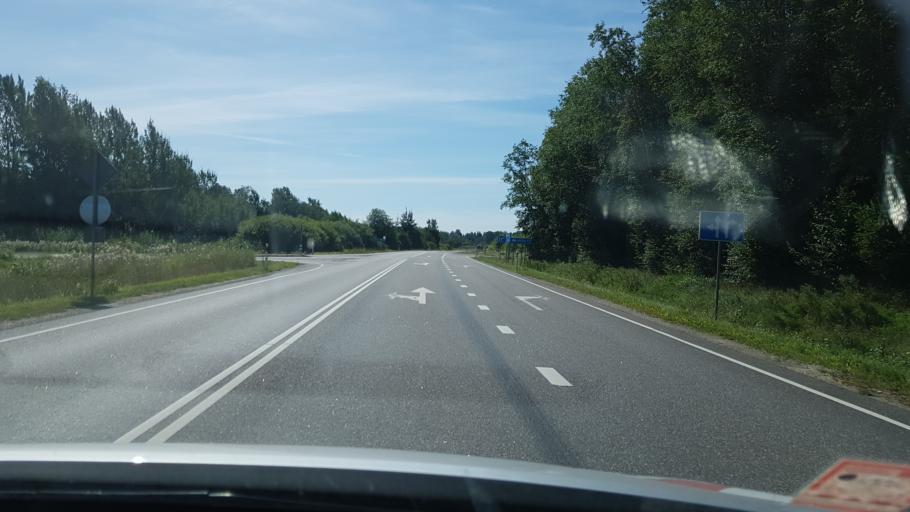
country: EE
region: Tartu
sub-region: Tartu linn
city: Tartu
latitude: 58.4055
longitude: 26.8959
